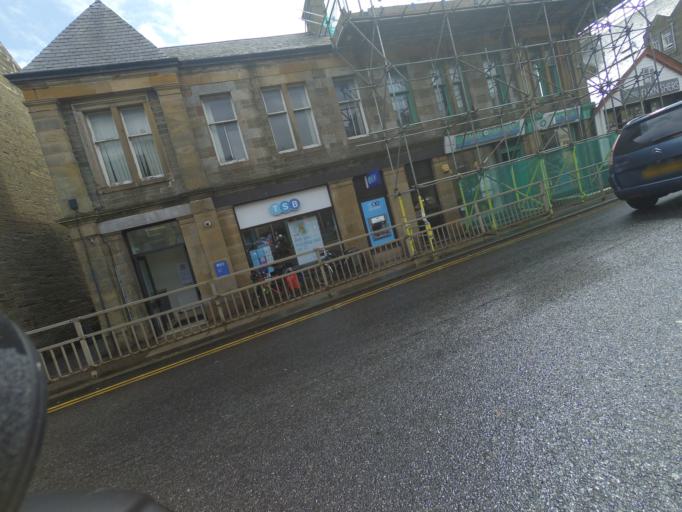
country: GB
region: Scotland
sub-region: Highland
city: Thurso
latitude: 58.5945
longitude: -3.5207
